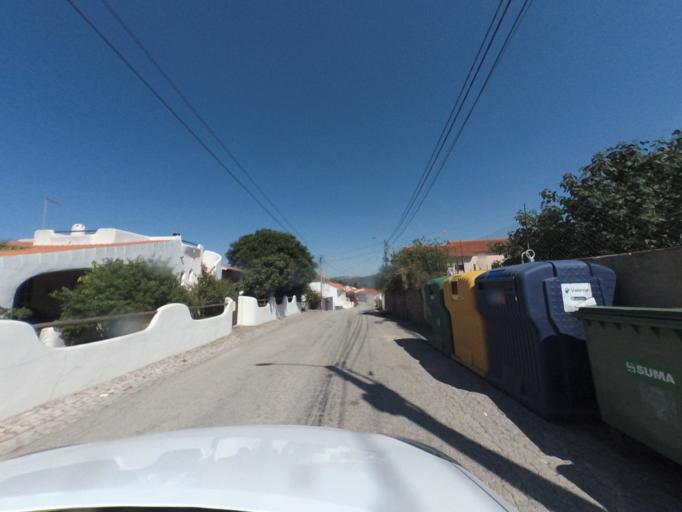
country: PT
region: Leiria
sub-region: Alcobaca
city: Turquel
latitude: 39.4666
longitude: -8.9795
